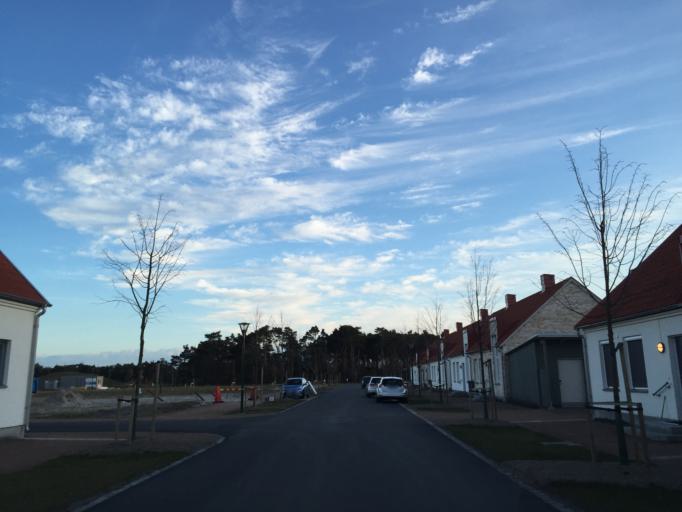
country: SE
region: Skane
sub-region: Vellinge Kommun
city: Skanor med Falsterbo
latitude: 55.4146
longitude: 12.8619
